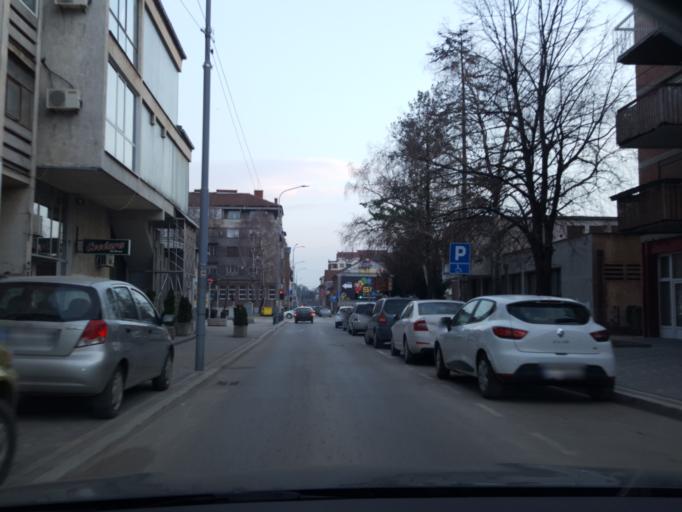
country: RS
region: Central Serbia
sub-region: Nisavski Okrug
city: Aleksinac
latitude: 43.5411
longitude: 21.7078
